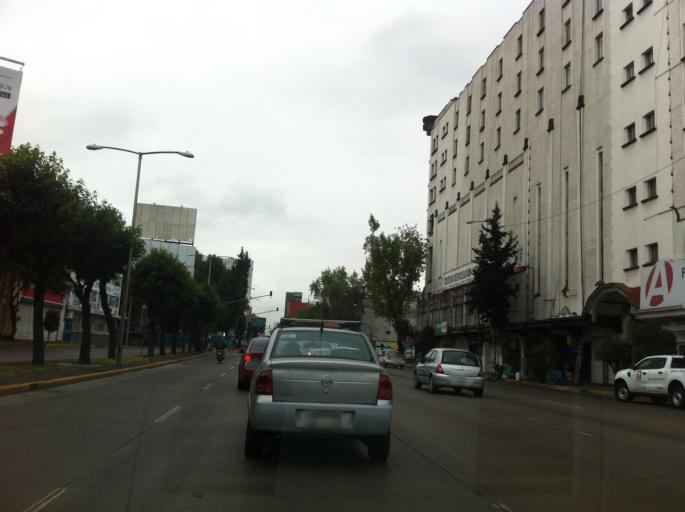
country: MX
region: Mexico City
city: Polanco
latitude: 19.4076
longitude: -99.1843
